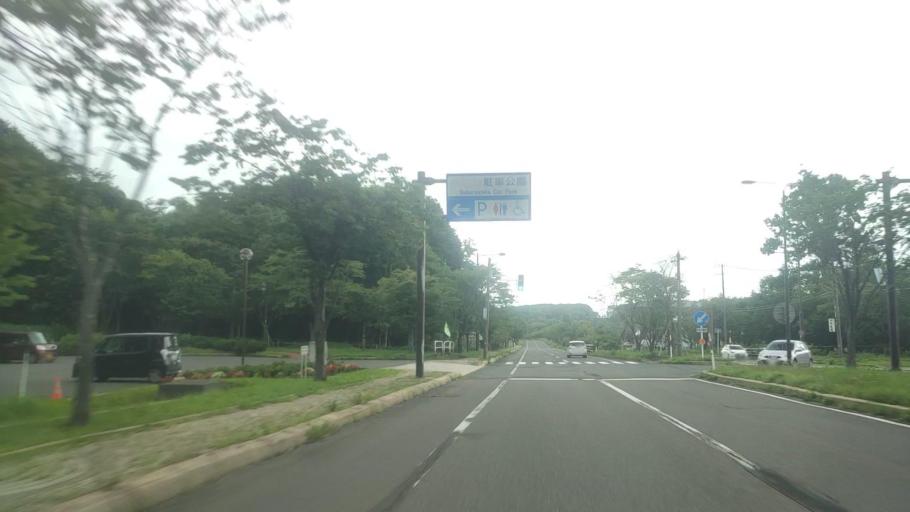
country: JP
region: Hokkaido
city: Shiraoi
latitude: 42.4665
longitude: 141.1673
